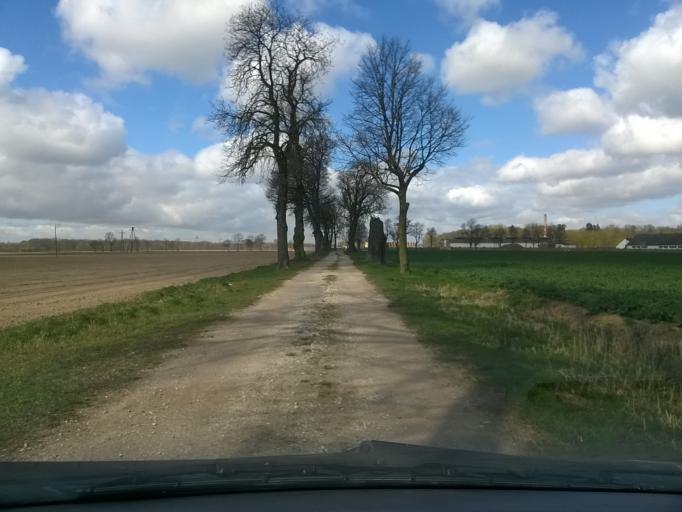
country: PL
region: Kujawsko-Pomorskie
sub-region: Powiat nakielski
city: Kcynia
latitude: 52.9846
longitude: 17.4305
